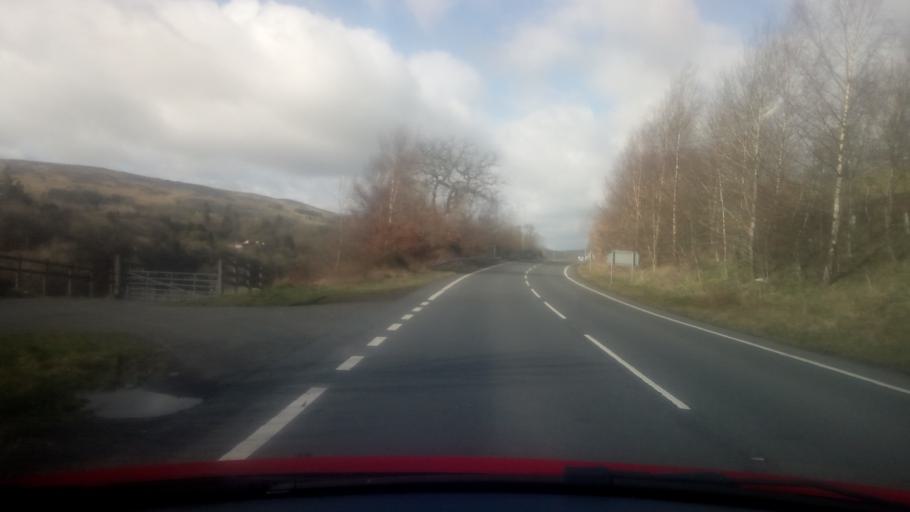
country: GB
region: Scotland
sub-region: The Scottish Borders
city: Selkirk
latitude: 55.6069
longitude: -2.8952
